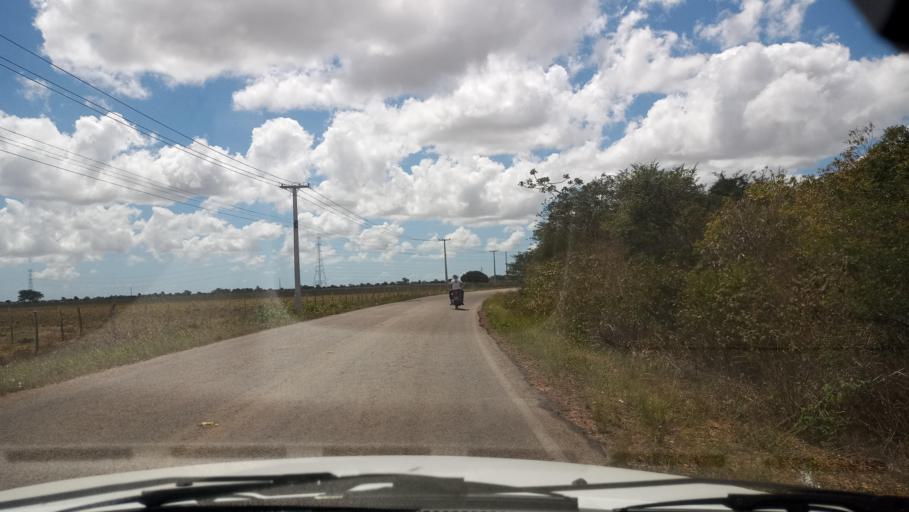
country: BR
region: Rio Grande do Norte
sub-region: Brejinho
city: Brejinho
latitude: -6.0404
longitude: -35.4167
